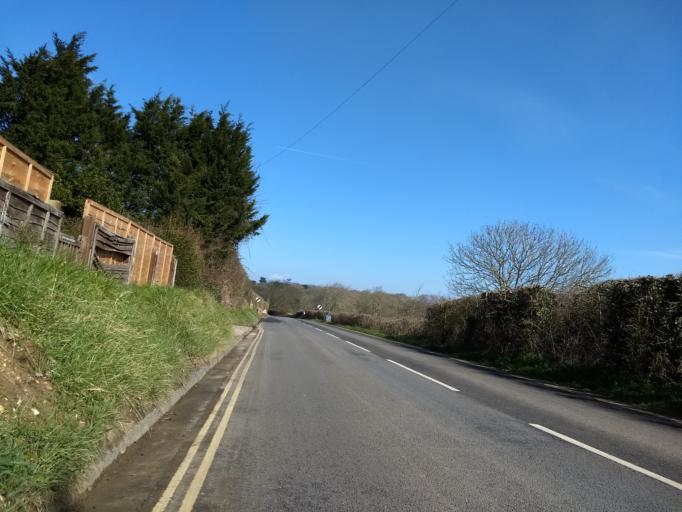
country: GB
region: England
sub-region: Isle of Wight
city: Seaview
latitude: 50.7005
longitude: -1.1078
